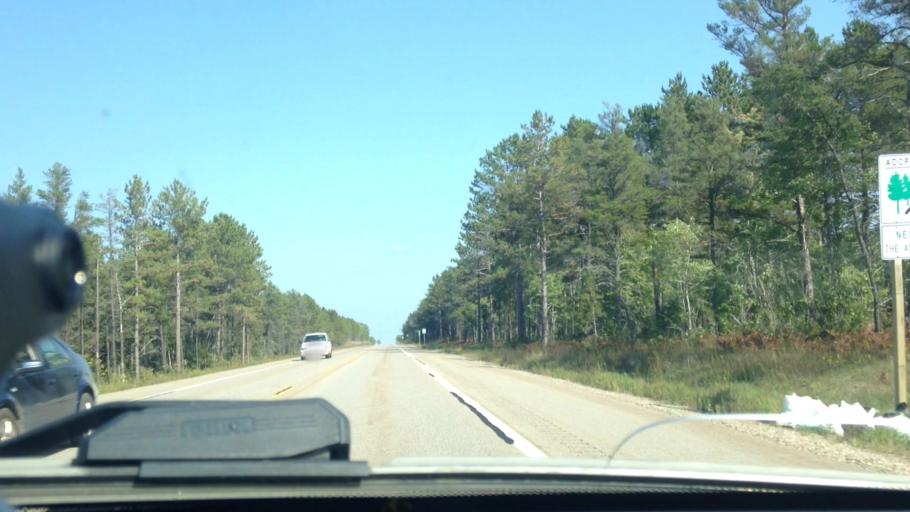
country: US
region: Michigan
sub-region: Chippewa County
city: Sault Ste. Marie
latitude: 46.3607
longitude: -84.7834
